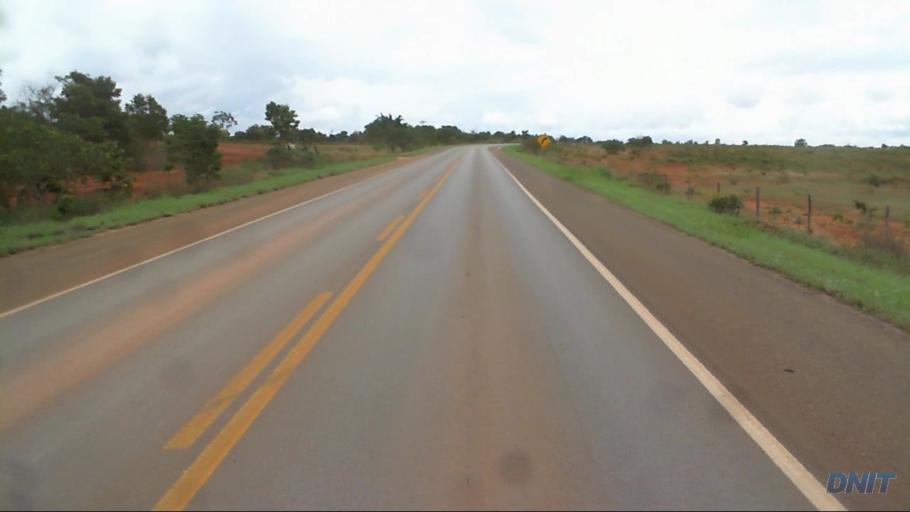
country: BR
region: Goias
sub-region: Padre Bernardo
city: Padre Bernardo
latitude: -15.1528
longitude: -48.3508
